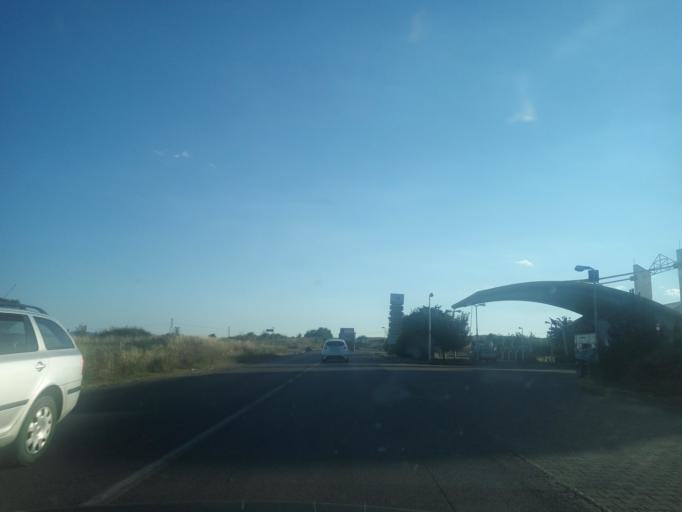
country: XK
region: Gjakova
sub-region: Komuna e Gjakoves
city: Gjakove
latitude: 42.4531
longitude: 20.5016
